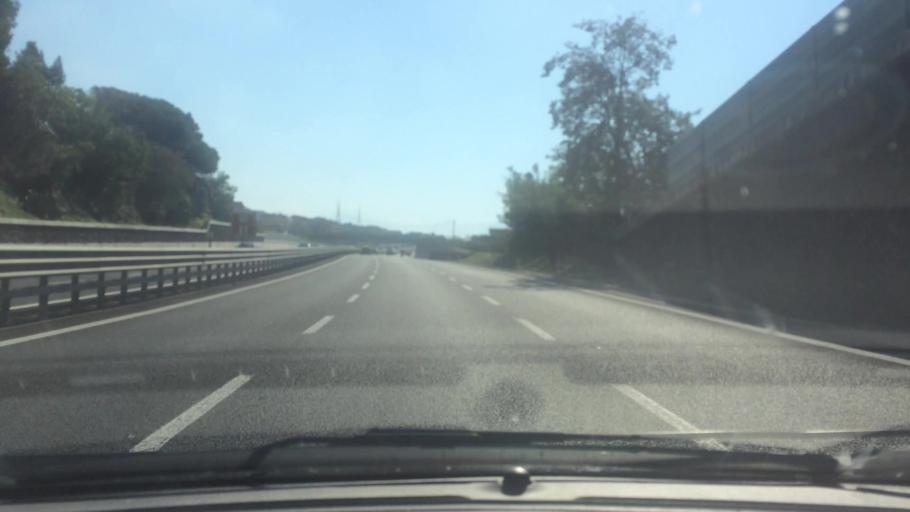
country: IT
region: Campania
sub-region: Provincia di Napoli
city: Ercolano
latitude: 40.8133
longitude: 14.3581
